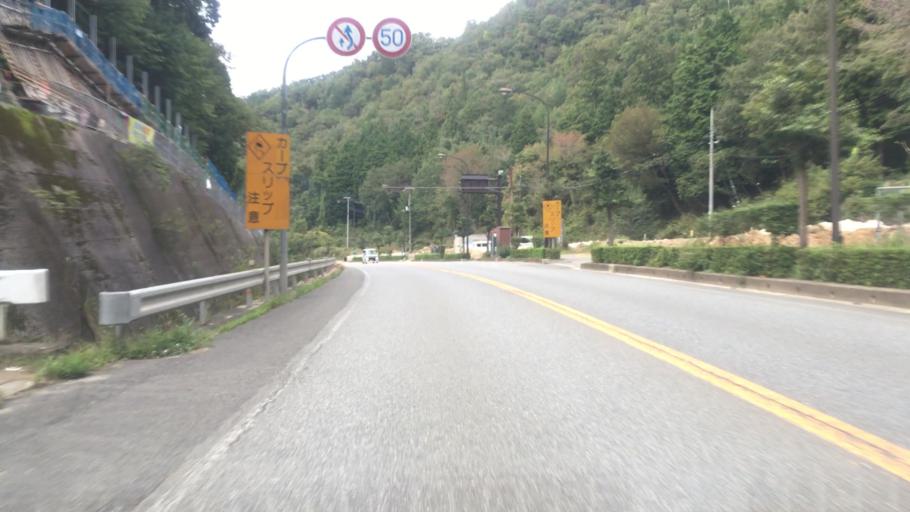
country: JP
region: Hyogo
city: Toyooka
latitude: 35.3956
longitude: 134.7728
